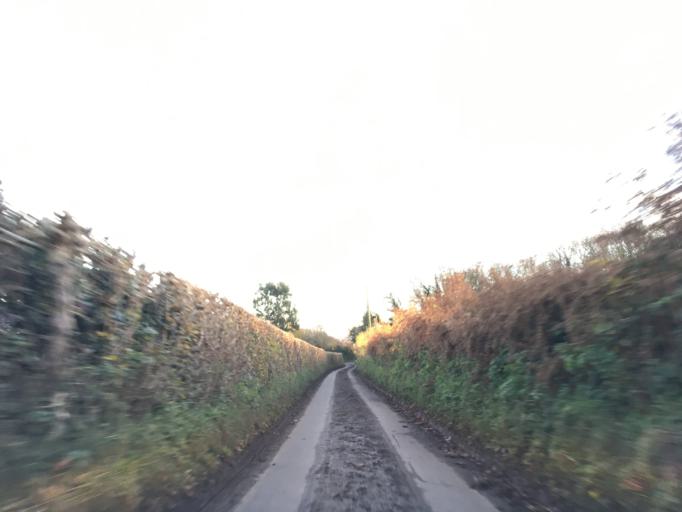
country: GB
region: England
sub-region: South Gloucestershire
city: Tytherington
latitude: 51.6009
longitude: -2.4677
